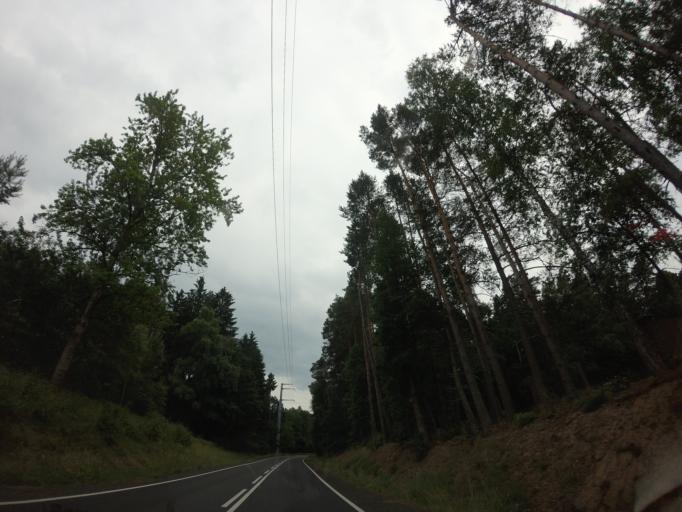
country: PL
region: West Pomeranian Voivodeship
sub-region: Powiat drawski
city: Czaplinek
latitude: 53.5066
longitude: 16.2232
